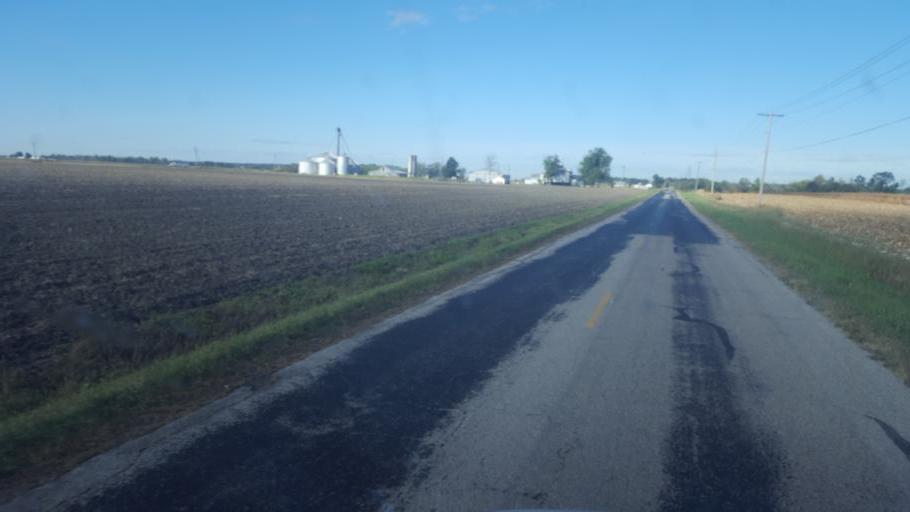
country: US
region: Ohio
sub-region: Marion County
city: Marion
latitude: 40.6882
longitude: -83.1237
